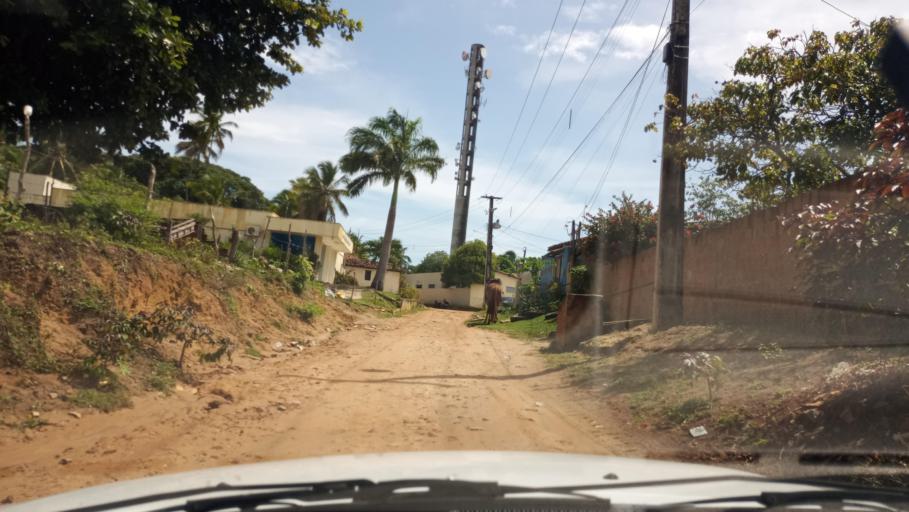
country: BR
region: Rio Grande do Norte
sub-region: Maxaranguape
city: Sao Miguel
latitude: -5.4621
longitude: -35.2933
